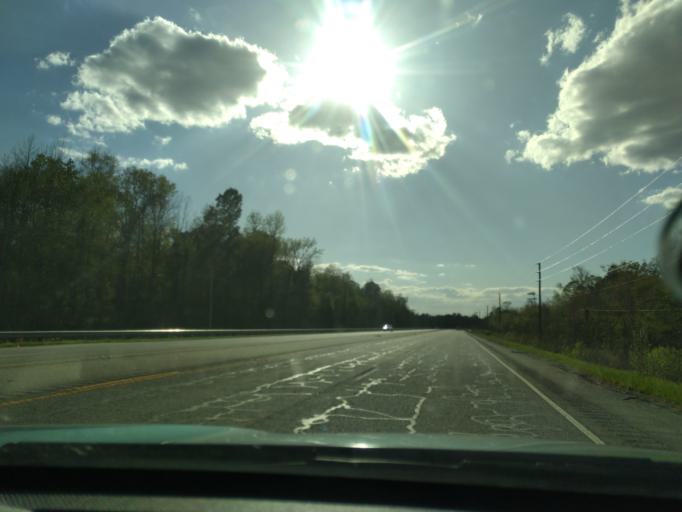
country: US
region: South Carolina
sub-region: Williamsburg County
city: Kingstree
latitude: 33.6578
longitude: -79.8671
